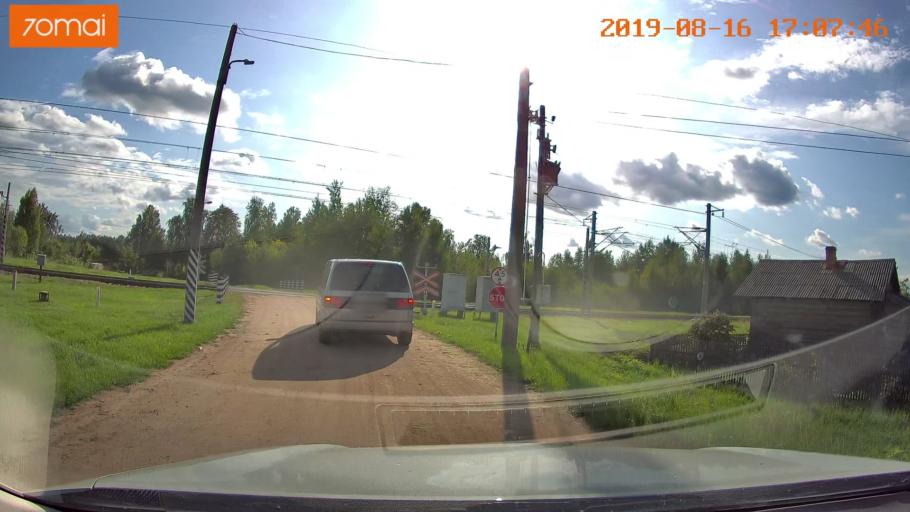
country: BY
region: Mogilev
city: Hlusha
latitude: 53.2220
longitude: 28.9228
